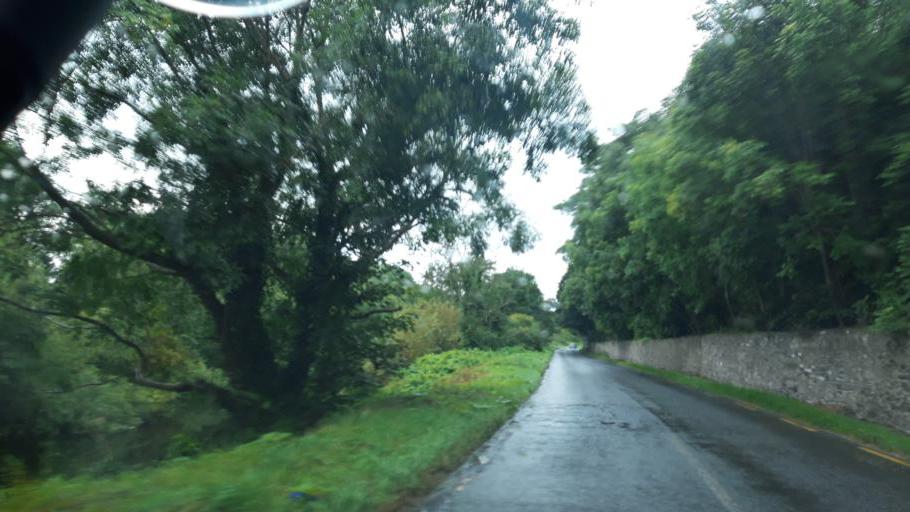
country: IE
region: Leinster
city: Hartstown
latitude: 53.3684
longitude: -6.4146
